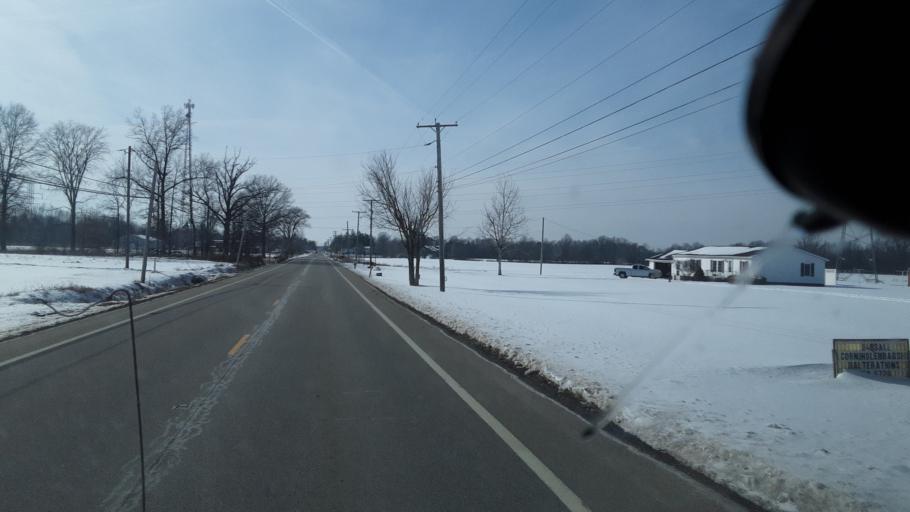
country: US
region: Ohio
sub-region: Mahoning County
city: Craig Beach
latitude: 41.0245
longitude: -80.9365
